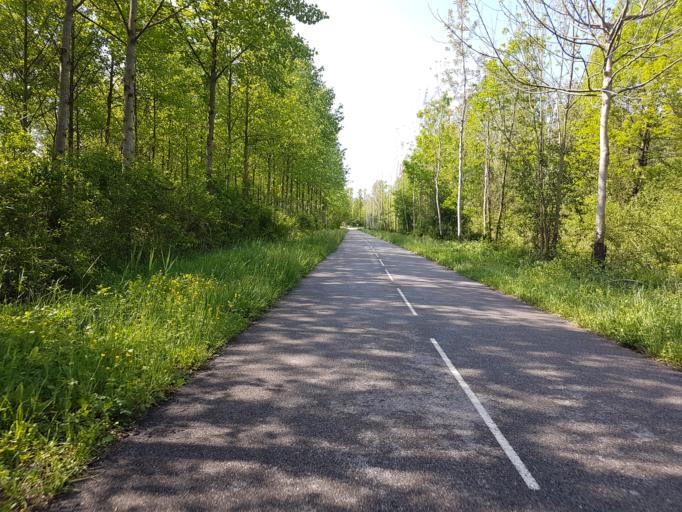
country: FR
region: Rhone-Alpes
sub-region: Departement de l'Ain
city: Culoz
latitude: 45.8535
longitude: 5.8203
